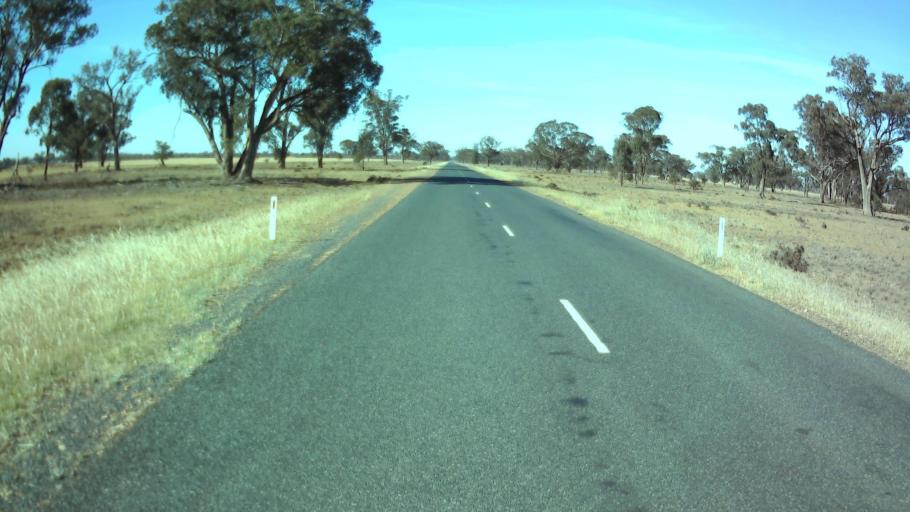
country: AU
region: New South Wales
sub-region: Weddin
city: Grenfell
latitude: -34.0799
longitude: 147.8967
